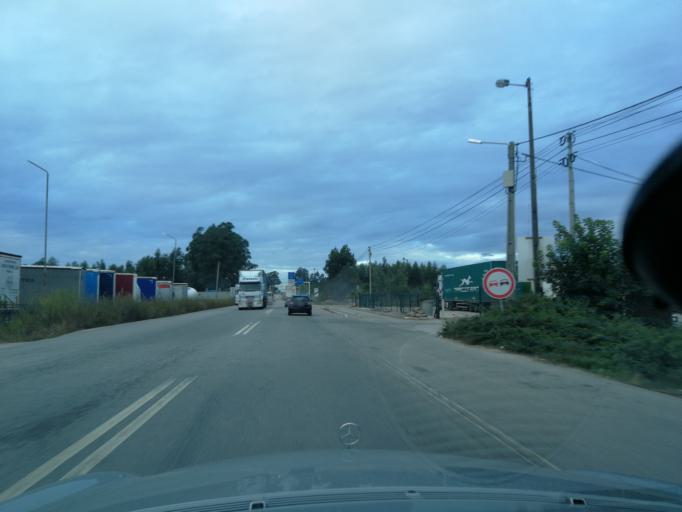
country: PT
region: Aveiro
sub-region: Albergaria-A-Velha
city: Albergaria-a-Velha
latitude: 40.6704
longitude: -8.4740
